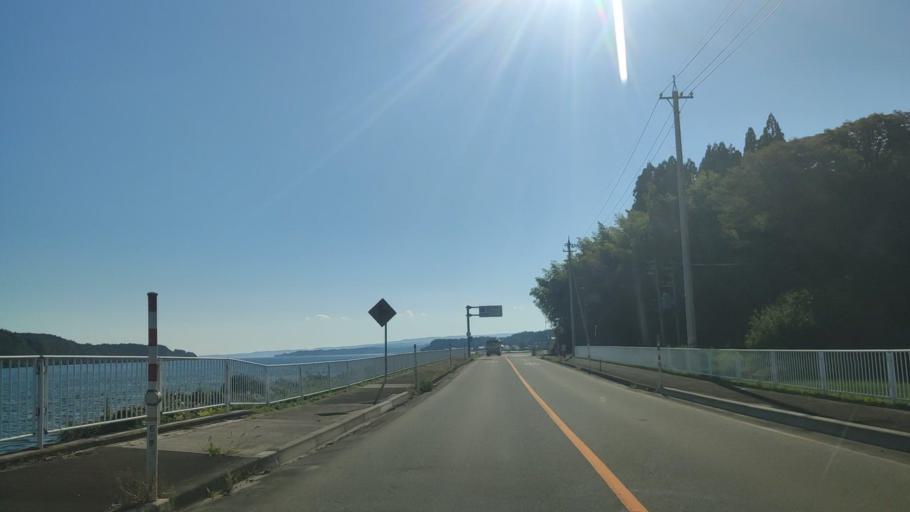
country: JP
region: Ishikawa
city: Nanao
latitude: 37.2360
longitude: 136.9590
